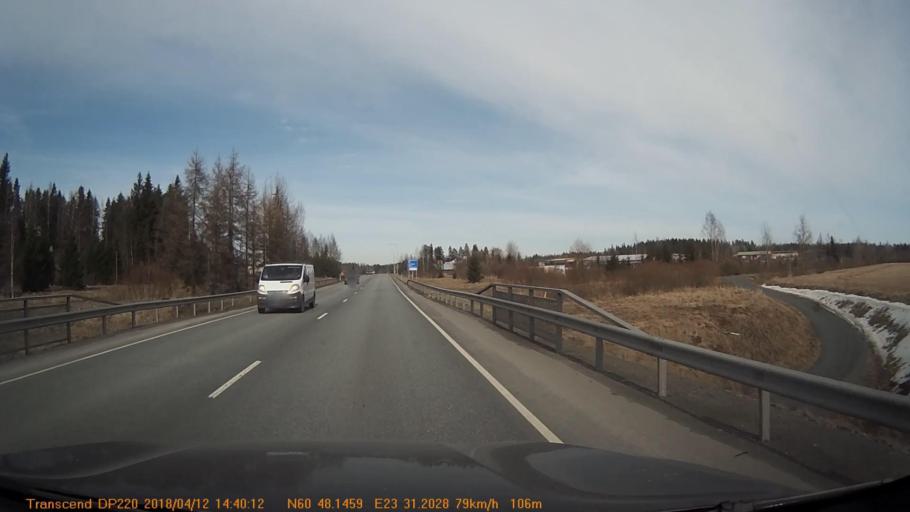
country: FI
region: Haeme
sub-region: Forssa
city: Jokioinen
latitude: 60.8035
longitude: 23.5220
